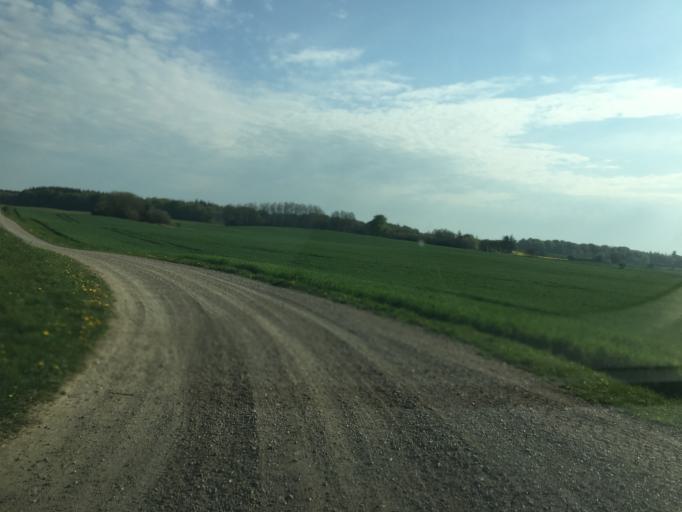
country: DK
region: South Denmark
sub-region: Aabenraa Kommune
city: Lojt Kirkeby
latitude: 55.1559
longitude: 9.3883
